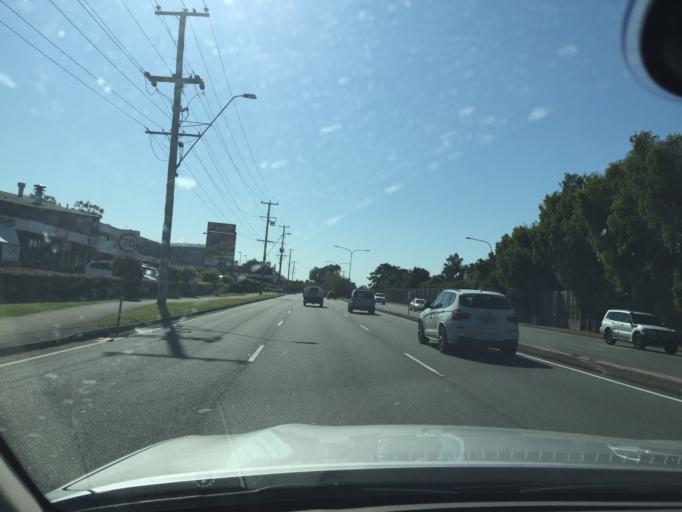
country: AU
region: Queensland
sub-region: Gold Coast
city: Clear Island Waters
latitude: -28.0316
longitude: 153.3924
